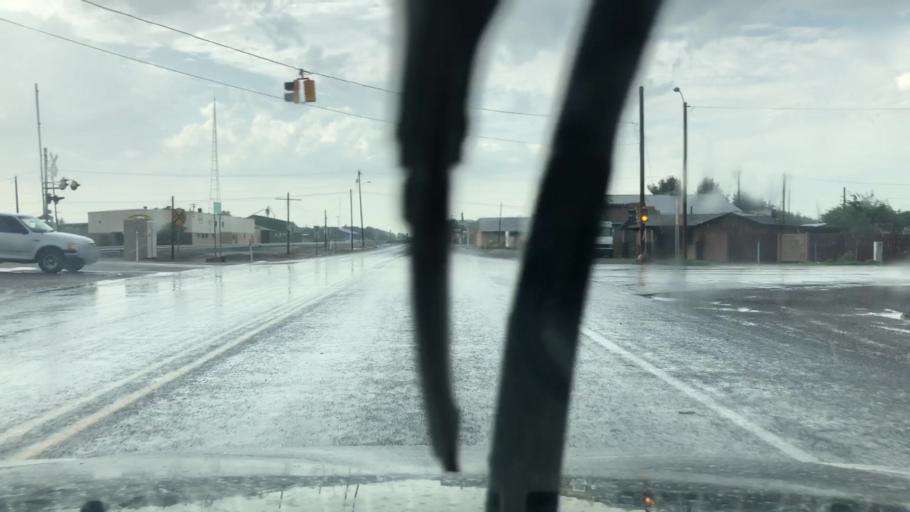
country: US
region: New Mexico
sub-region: Dona Ana County
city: Mesquite
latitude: 32.1635
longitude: -106.6959
